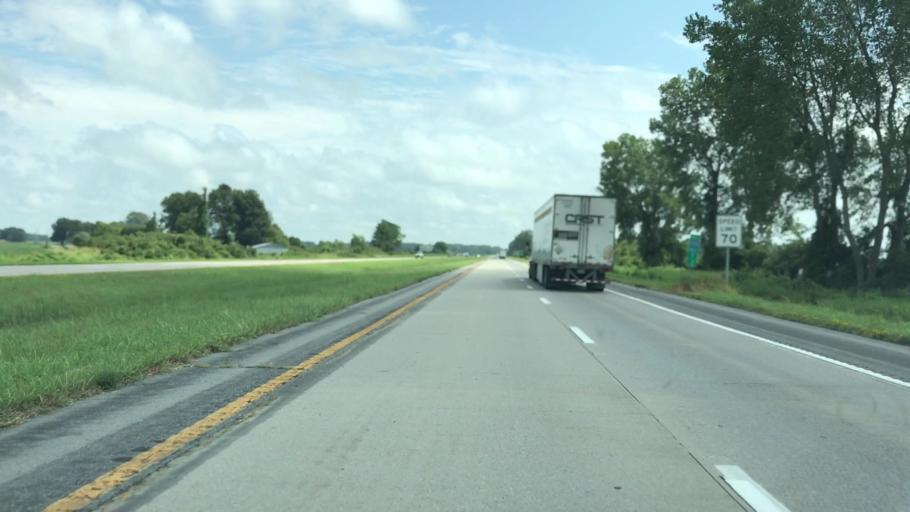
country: US
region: Missouri
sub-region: Pemiscot County
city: Caruthersville
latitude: 36.1476
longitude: -89.6547
